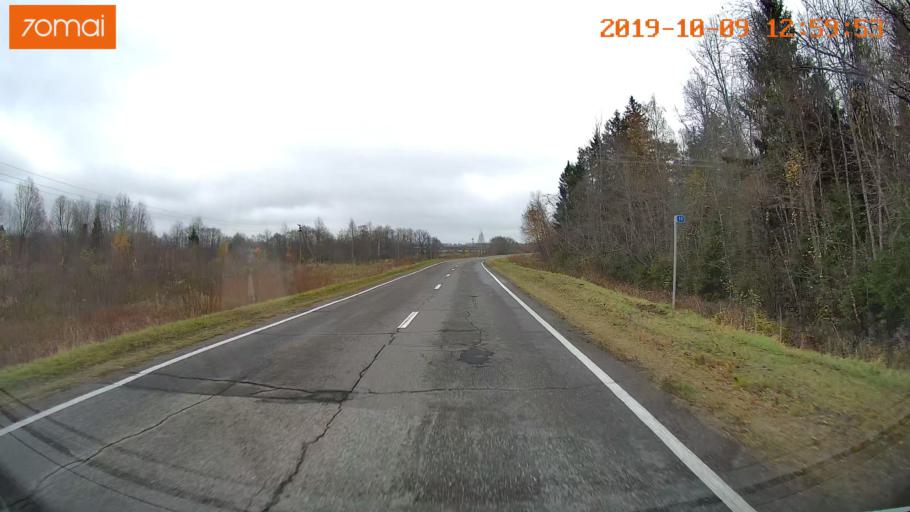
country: RU
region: Jaroslavl
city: Prechistoye
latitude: 58.3815
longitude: 40.4721
